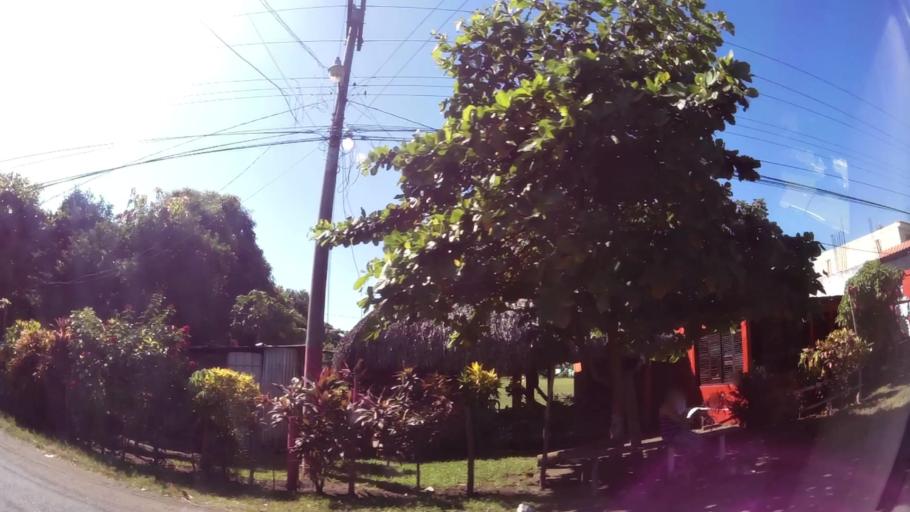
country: GT
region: Escuintla
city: Iztapa
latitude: 13.9168
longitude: -90.5511
